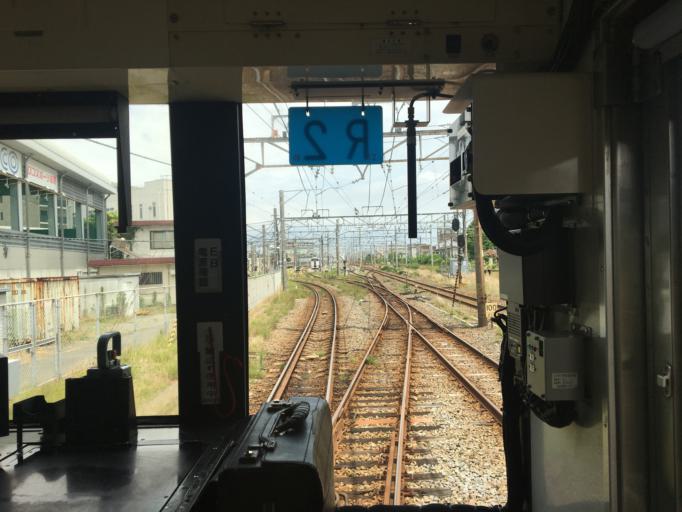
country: JP
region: Kanagawa
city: Chigasaki
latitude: 35.3314
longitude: 139.4093
